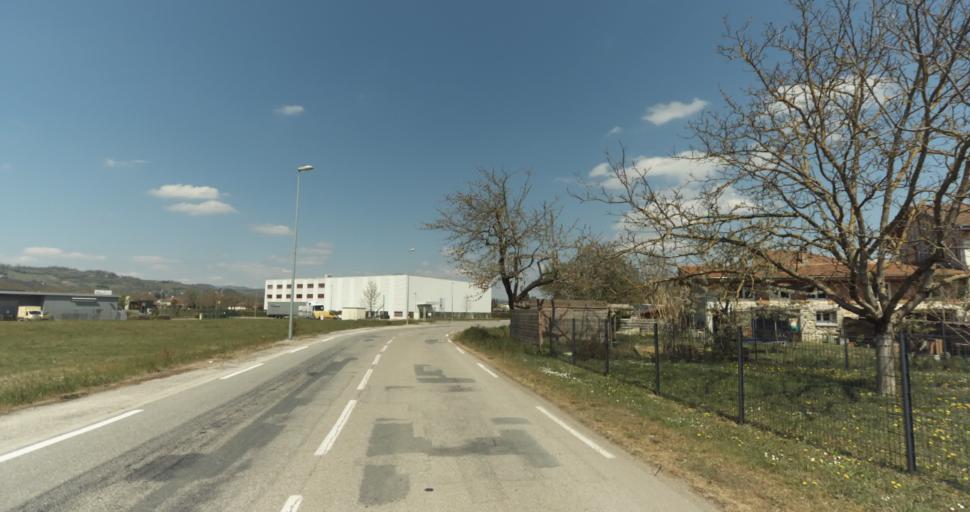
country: FR
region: Rhone-Alpes
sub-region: Departement de l'Isere
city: Saint-Marcellin
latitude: 45.1374
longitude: 5.3221
